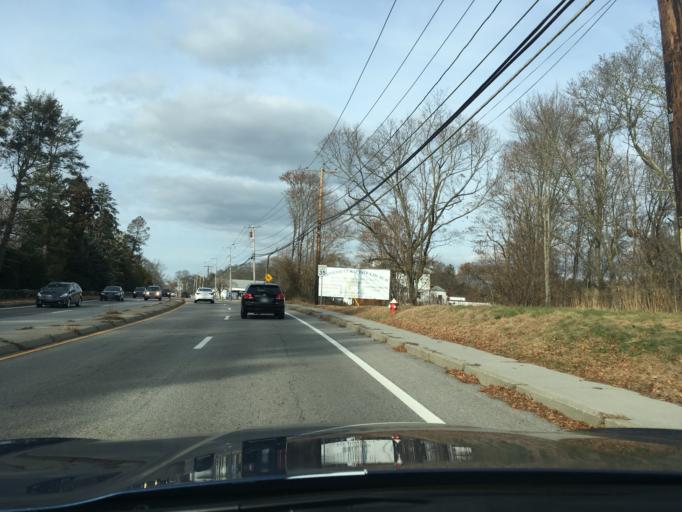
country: US
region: Rhode Island
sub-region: Kent County
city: East Greenwich
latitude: 41.6232
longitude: -71.4585
